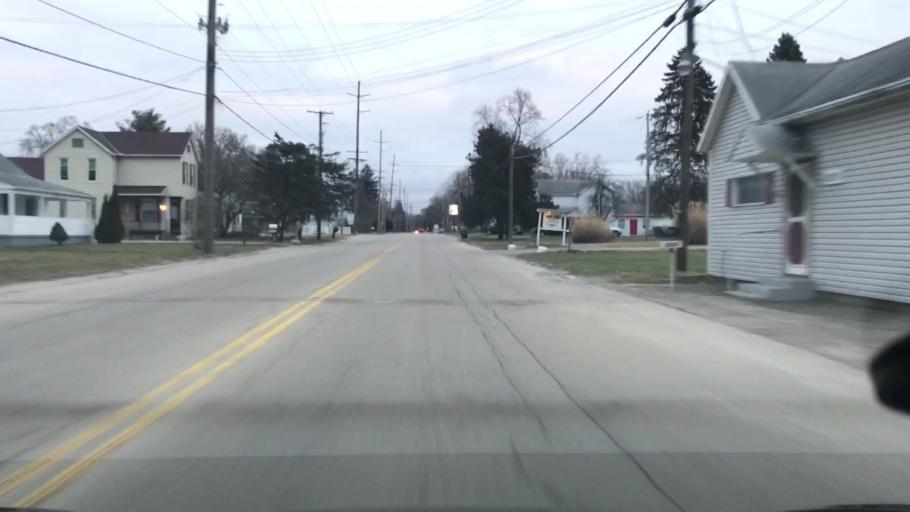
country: US
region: Ohio
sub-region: Clark County
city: Springfield
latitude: 39.9368
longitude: -83.7628
